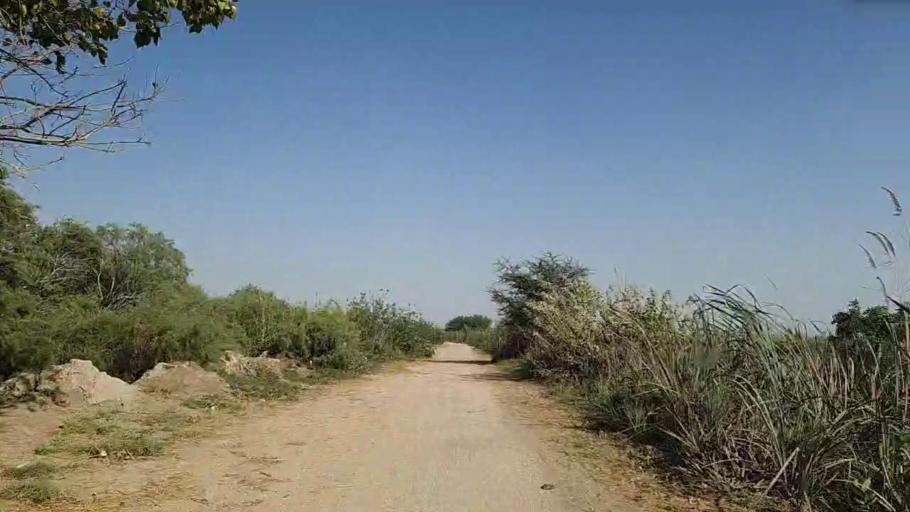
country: PK
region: Sindh
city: Chuhar Jamali
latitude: 24.4817
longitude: 68.1027
